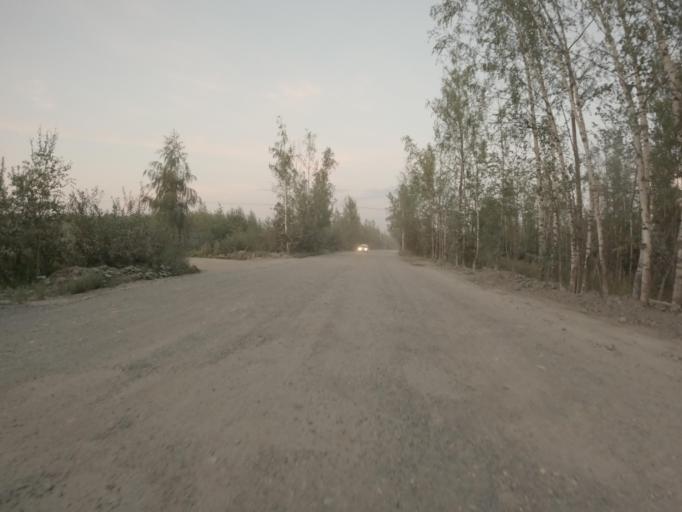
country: RU
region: Leningrad
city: Yanino Vtoroye
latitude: 59.9421
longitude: 30.5995
